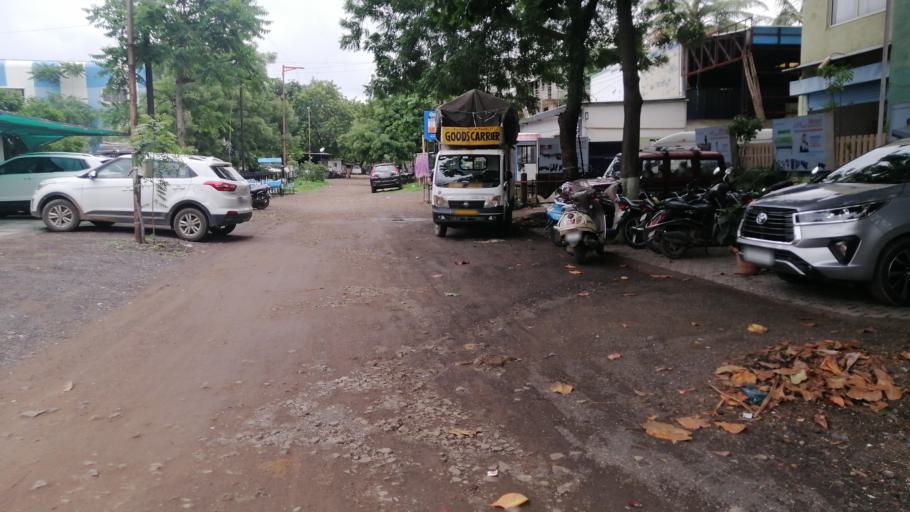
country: IN
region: Maharashtra
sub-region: Aurangabad Division
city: Aurangabad
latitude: 19.8809
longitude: 75.3756
